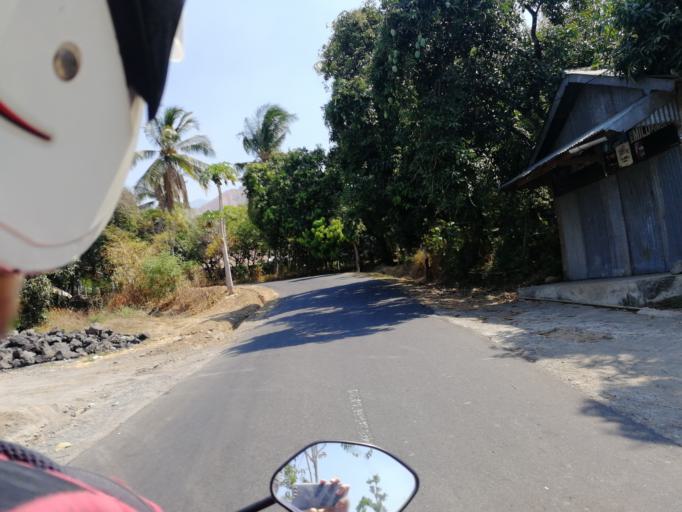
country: ID
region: Bali
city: Banjar Trunyan
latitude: -8.1254
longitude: 115.3290
